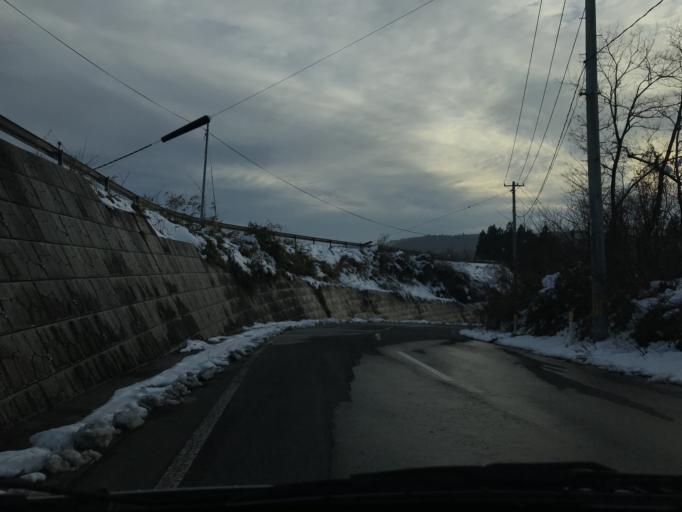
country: JP
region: Iwate
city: Mizusawa
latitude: 39.0588
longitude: 141.0873
